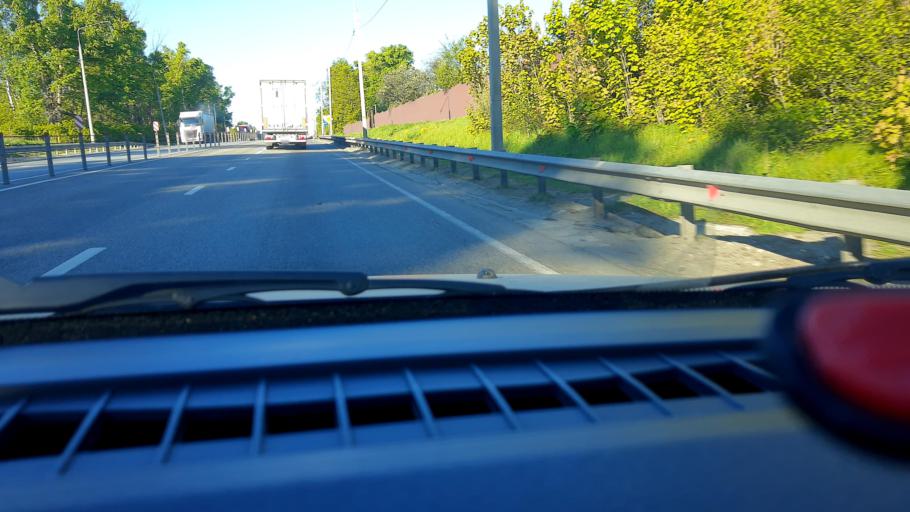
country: RU
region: Vladimir
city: Gorokhovets
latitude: 56.1880
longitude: 42.6784
